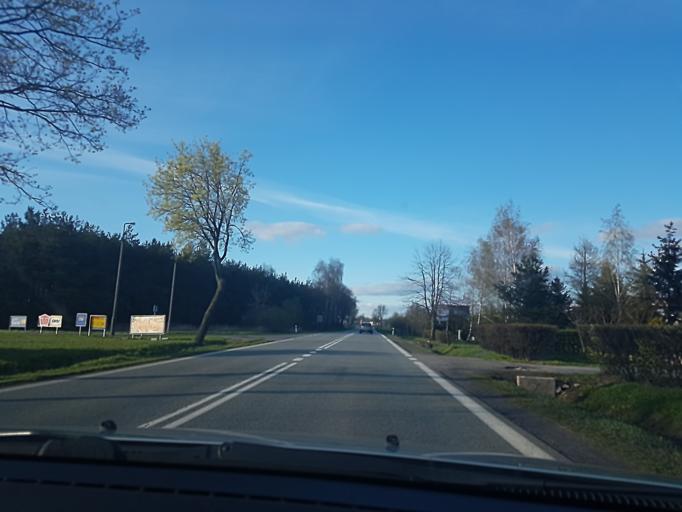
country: PL
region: Lodz Voivodeship
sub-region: Powiat kutnowski
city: Kutno
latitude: 52.2669
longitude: 19.3893
